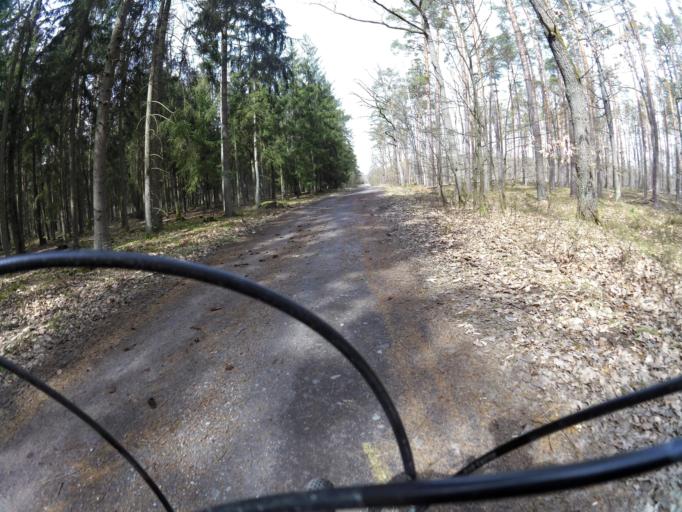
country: PL
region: West Pomeranian Voivodeship
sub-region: Powiat gryfinski
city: Mieszkowice
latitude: 52.7194
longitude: 14.4929
